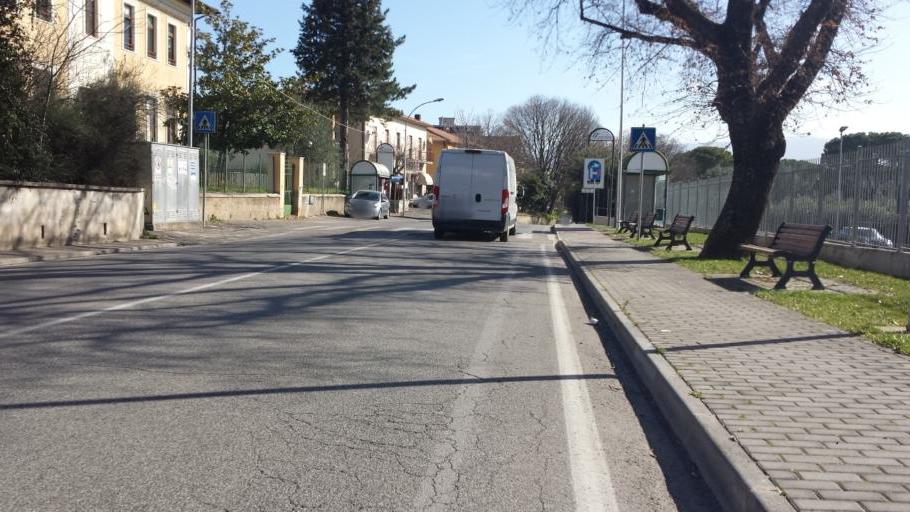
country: IT
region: Umbria
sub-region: Provincia di Terni
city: Terni
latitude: 42.5845
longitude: 12.6137
